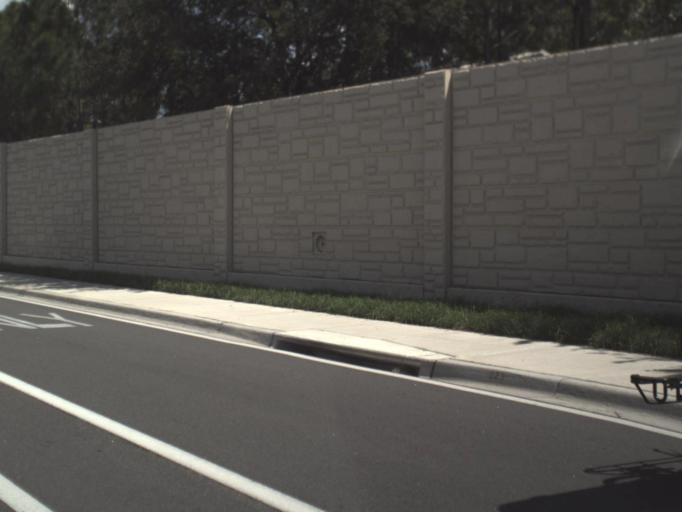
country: US
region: Florida
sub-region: Pinellas County
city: Ridgecrest
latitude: 27.8946
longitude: -82.7971
